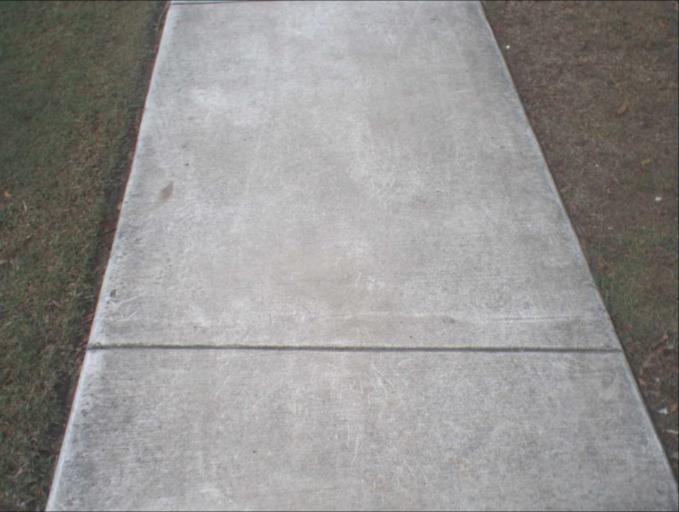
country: AU
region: Queensland
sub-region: Logan
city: Park Ridge South
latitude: -27.6850
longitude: 153.0416
